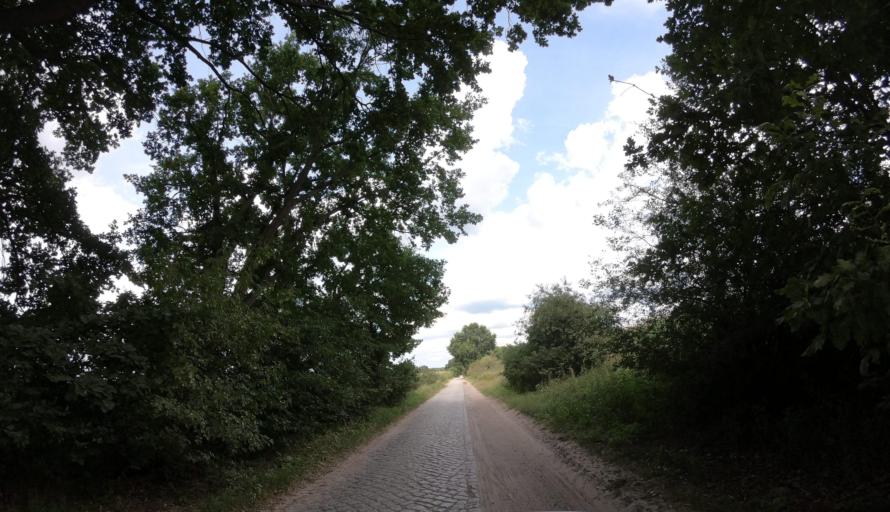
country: PL
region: West Pomeranian Voivodeship
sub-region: Powiat stargardzki
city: Kobylanka
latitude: 53.3144
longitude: 14.8295
